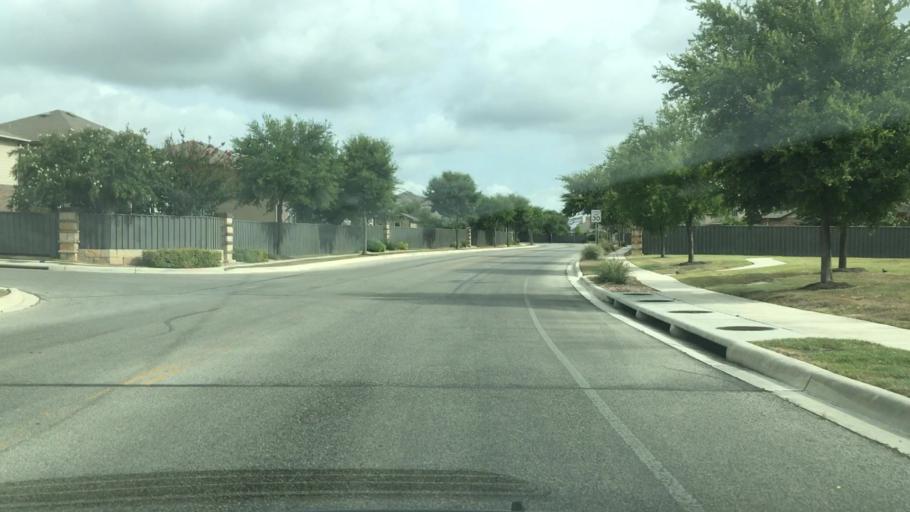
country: US
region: Texas
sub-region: Guadalupe County
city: Cibolo
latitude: 29.5788
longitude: -98.2397
